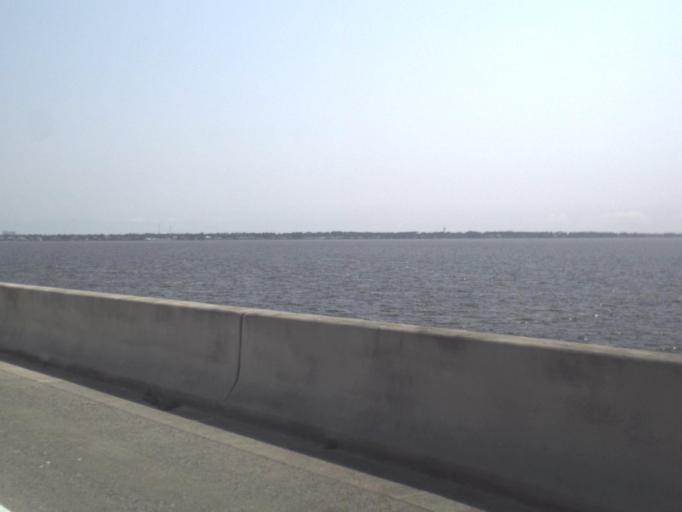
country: US
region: Florida
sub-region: Santa Rosa County
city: Oriole Beach
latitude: 30.4240
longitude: -87.0923
